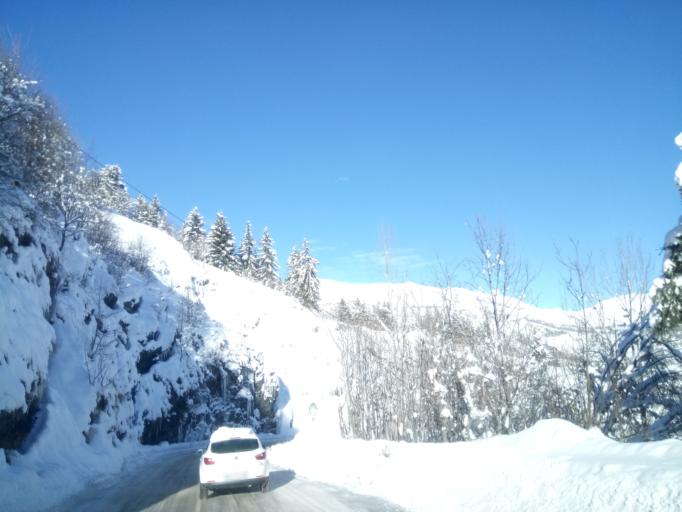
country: FR
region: Rhone-Alpes
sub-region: Departement de la Savoie
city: Saint-Jean-de-Maurienne
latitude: 45.2372
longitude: 6.2793
